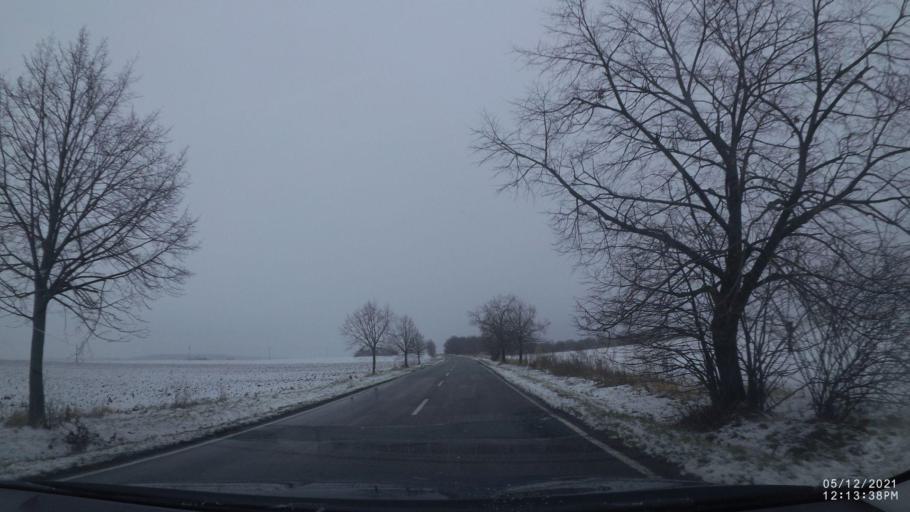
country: CZ
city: Ceske Mezirici
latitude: 50.3020
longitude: 16.0226
